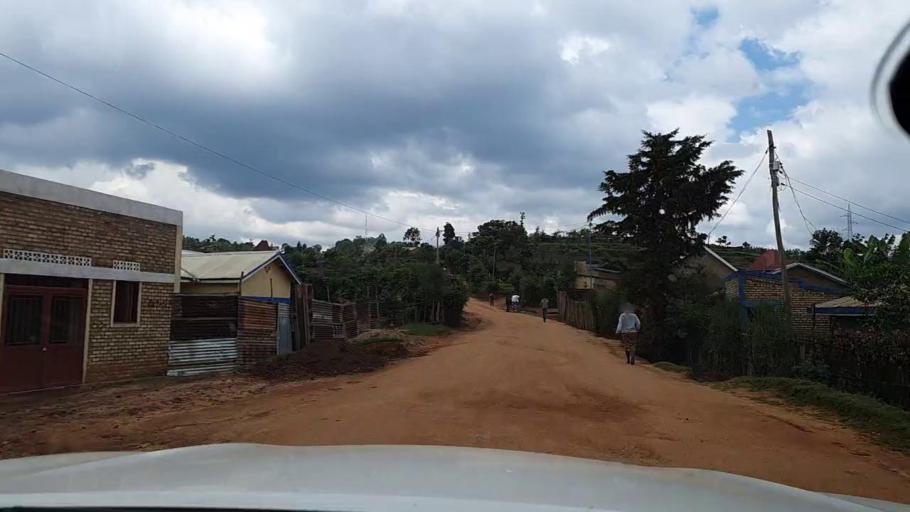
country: BI
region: Kayanza
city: Kayanza
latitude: -2.7116
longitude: 29.5327
